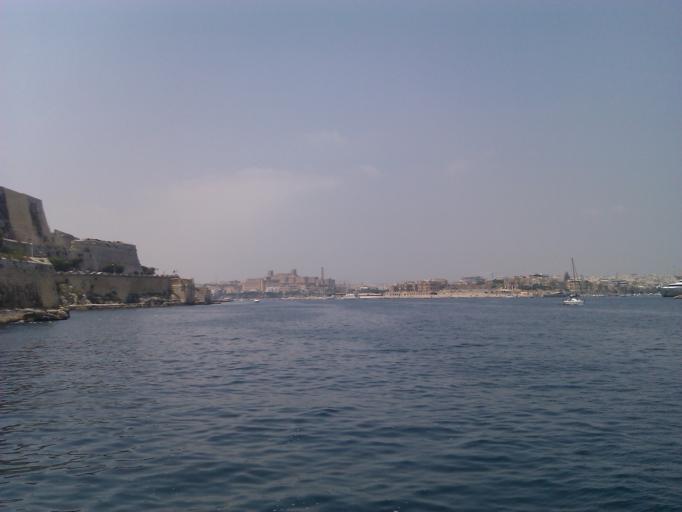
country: MT
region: Il-Furjana
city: Floriana
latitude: 35.9012
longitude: 14.5090
